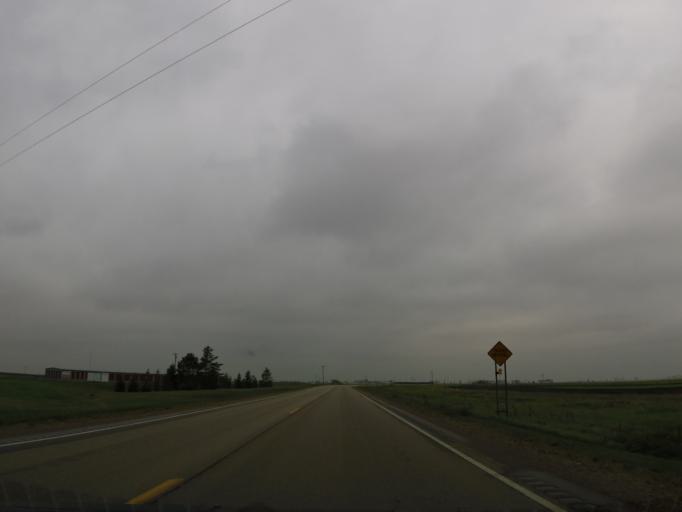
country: US
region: Minnesota
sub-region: Marshall County
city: Warren
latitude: 48.2058
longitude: -96.7759
